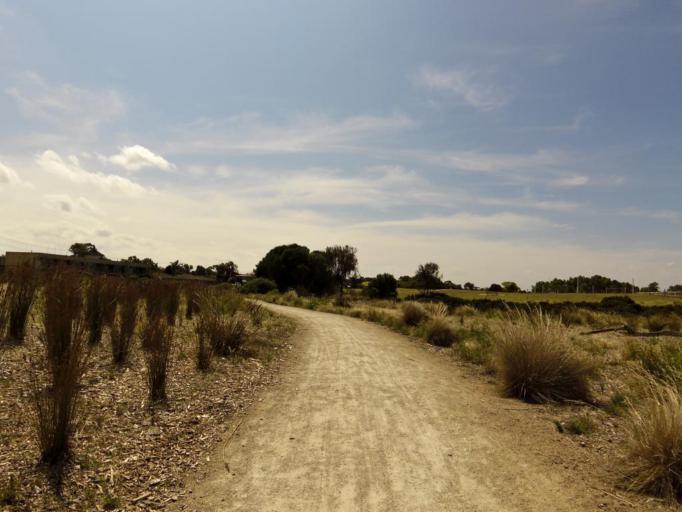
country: AU
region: Victoria
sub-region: Mornington Peninsula
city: Hastings
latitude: -38.3142
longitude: 145.1951
